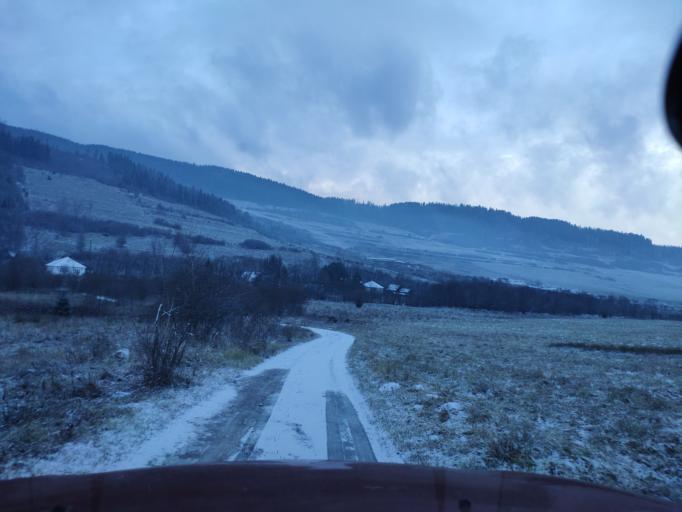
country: SK
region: Kosicky
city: Spisska Nova Ves
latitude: 48.8249
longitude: 20.6001
